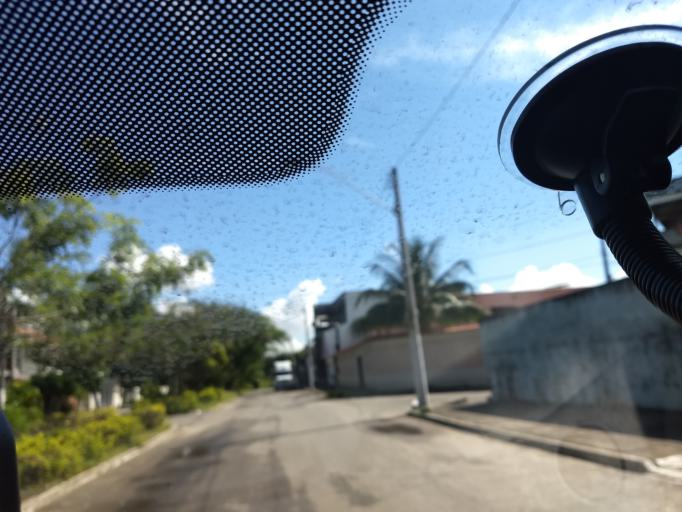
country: BR
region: Espirito Santo
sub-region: Vitoria
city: Vitoria
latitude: -20.3539
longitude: -40.3569
